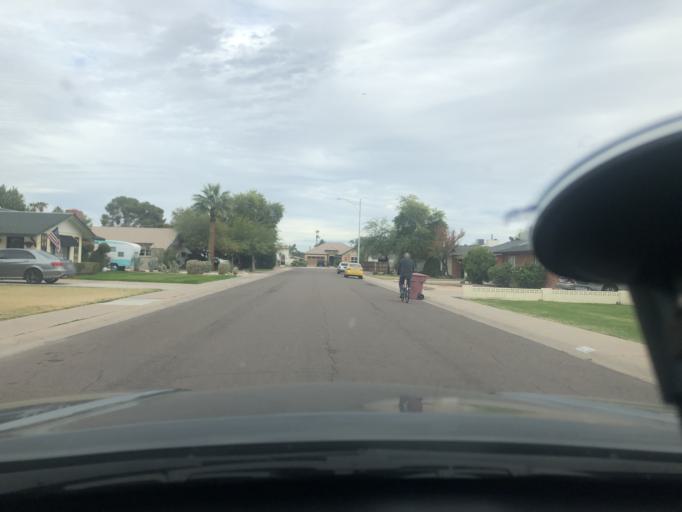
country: US
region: Arizona
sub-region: Maricopa County
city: Scottsdale
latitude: 33.4904
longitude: -111.9018
